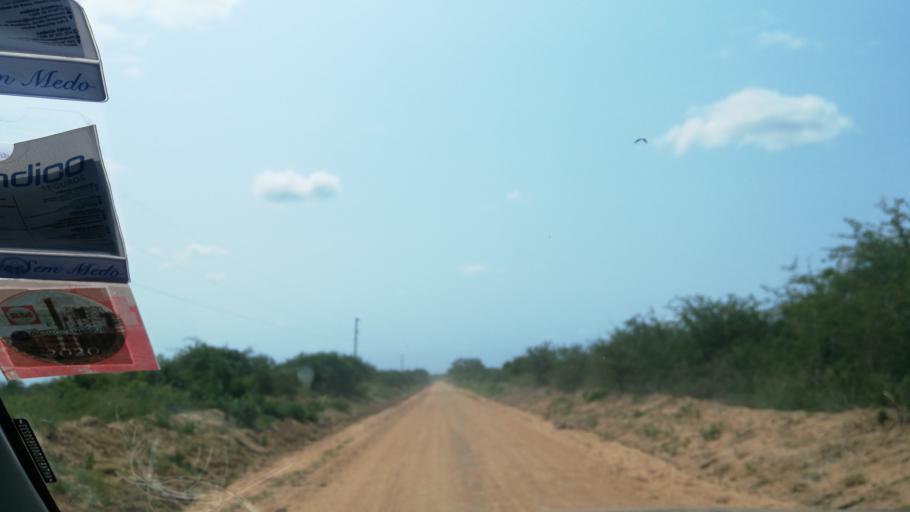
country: MZ
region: Maputo
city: Matola
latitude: -26.0925
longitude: 32.3907
